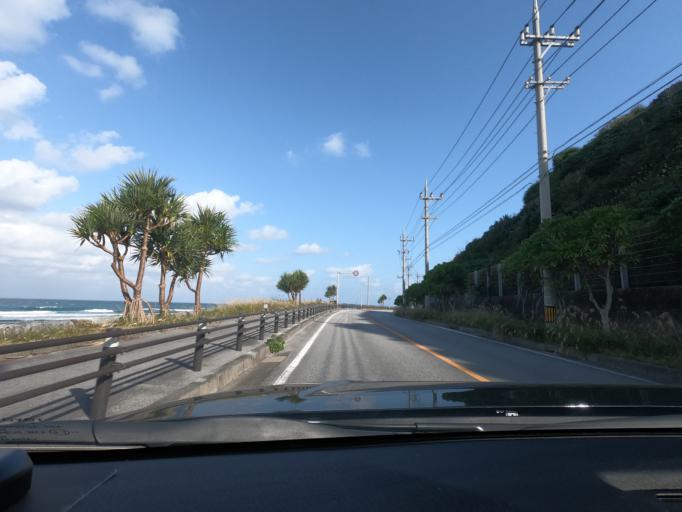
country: JP
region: Okinawa
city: Nago
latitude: 26.7597
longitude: 128.1894
